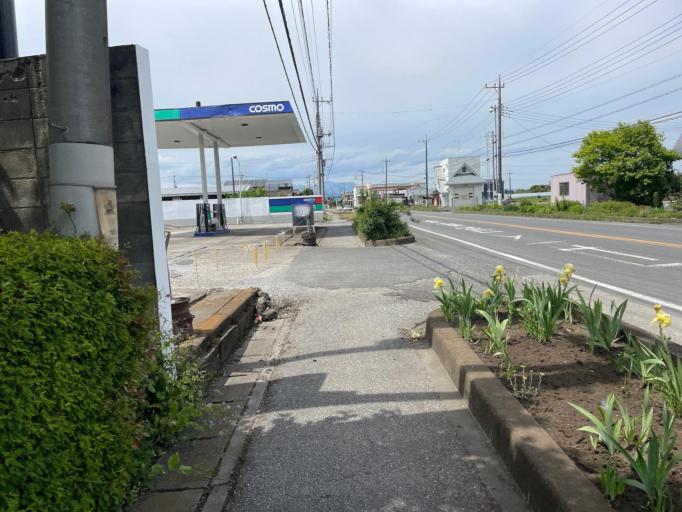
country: JP
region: Tochigi
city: Mibu
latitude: 36.4627
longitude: 139.7694
